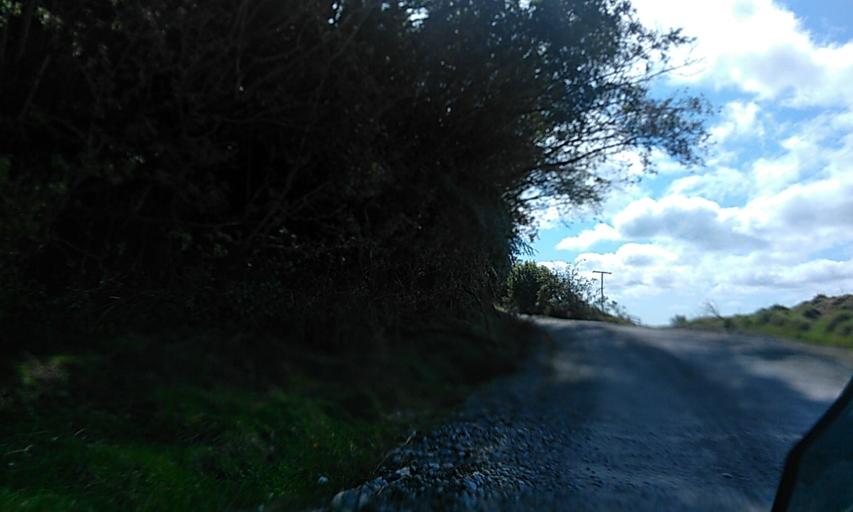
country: NZ
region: Gisborne
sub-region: Gisborne District
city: Gisborne
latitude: -38.2280
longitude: 178.0684
